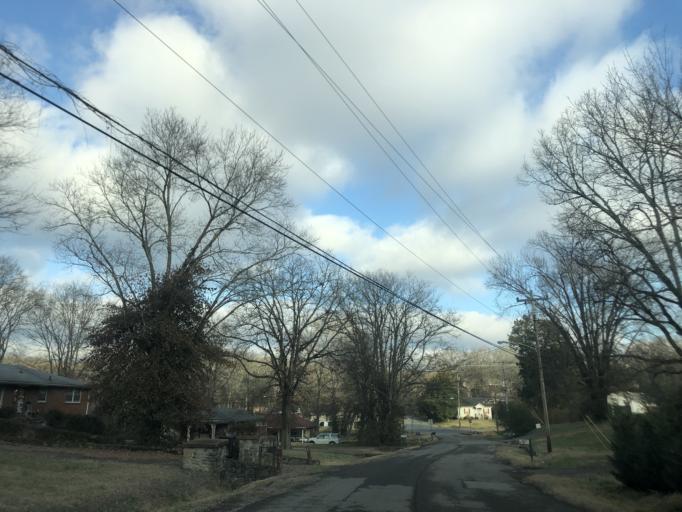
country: US
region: Tennessee
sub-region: Davidson County
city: Nashville
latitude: 36.2134
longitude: -86.8015
